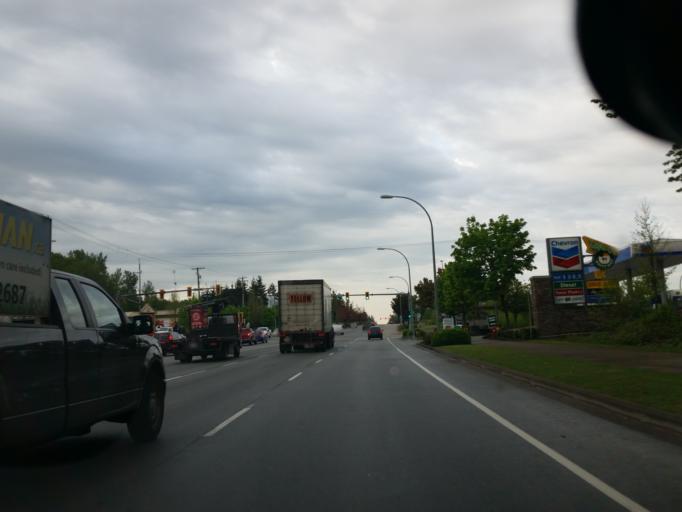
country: CA
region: British Columbia
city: Walnut Grove
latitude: 49.1603
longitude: -122.6682
